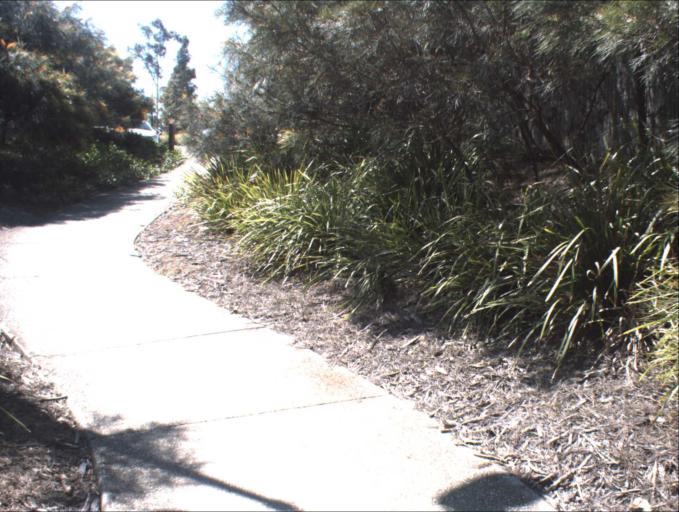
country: AU
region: Queensland
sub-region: Logan
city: Waterford West
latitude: -27.7159
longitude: 153.1509
